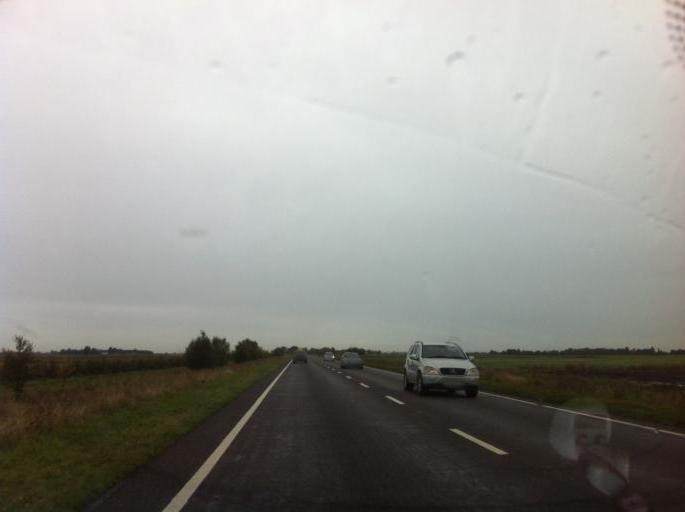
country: GB
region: England
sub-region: Peterborough
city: Eye
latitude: 52.6210
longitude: -0.2063
